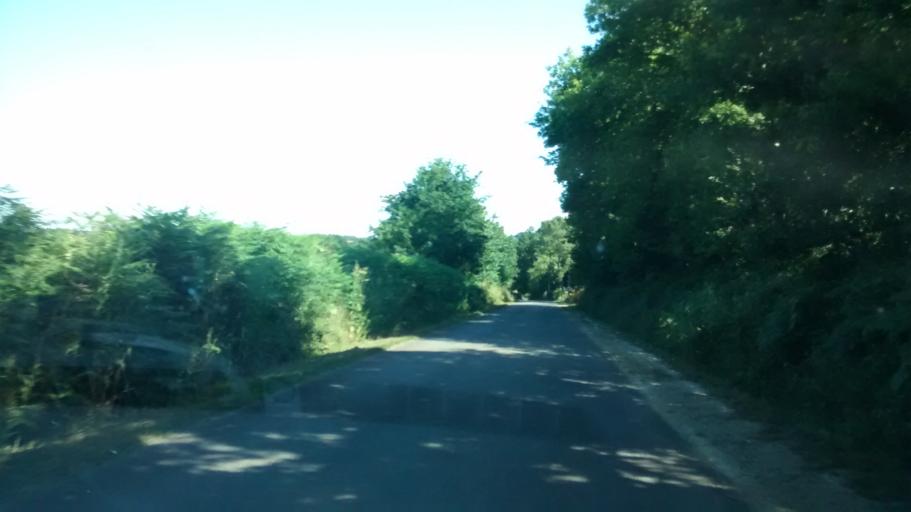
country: FR
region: Brittany
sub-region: Departement du Morbihan
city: Molac
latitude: 47.7855
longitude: -2.4383
